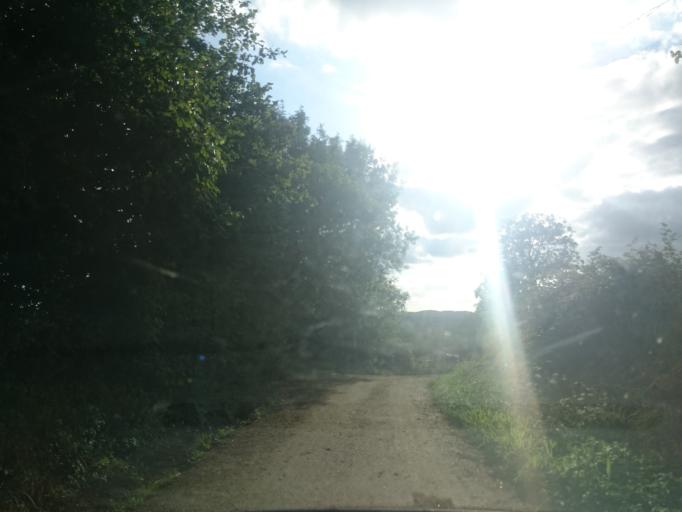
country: FR
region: Auvergne
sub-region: Departement du Cantal
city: Saint-Mamet-la-Salvetat
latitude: 44.8599
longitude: 2.2535
